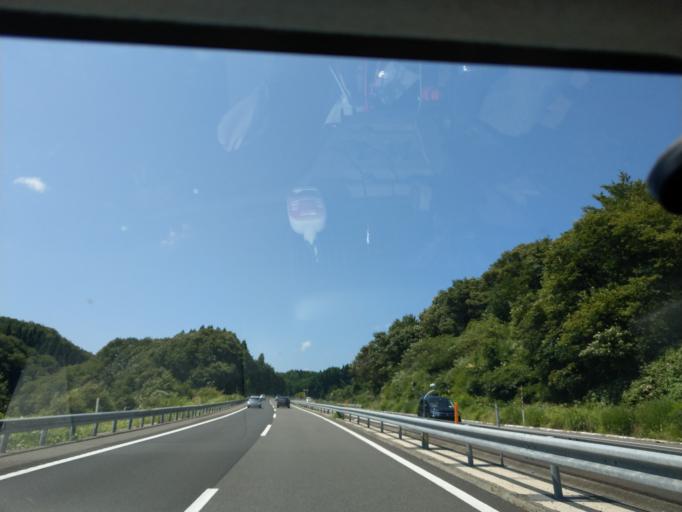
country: JP
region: Akita
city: Akita
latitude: 39.6079
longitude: 140.2568
